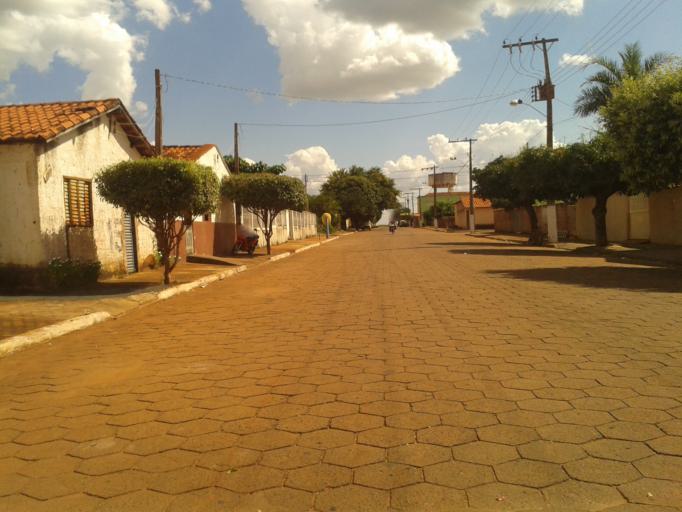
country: BR
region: Minas Gerais
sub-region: Santa Vitoria
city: Santa Vitoria
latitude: -18.6928
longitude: -49.9465
